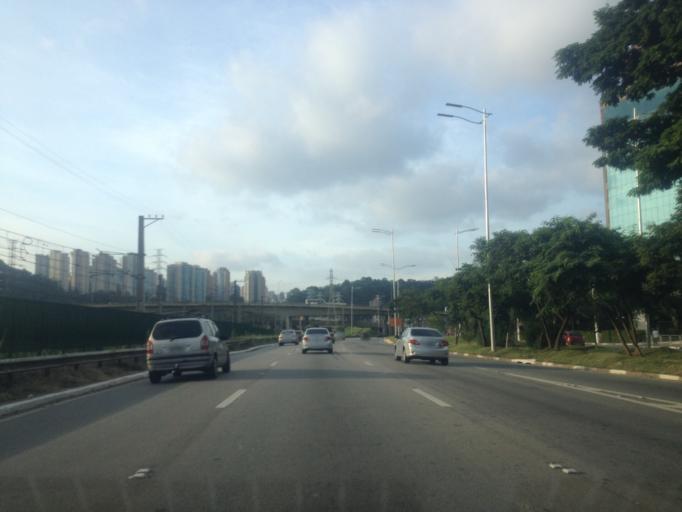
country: BR
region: Sao Paulo
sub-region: Taboao Da Serra
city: Taboao da Serra
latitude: -23.6474
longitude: -46.7253
